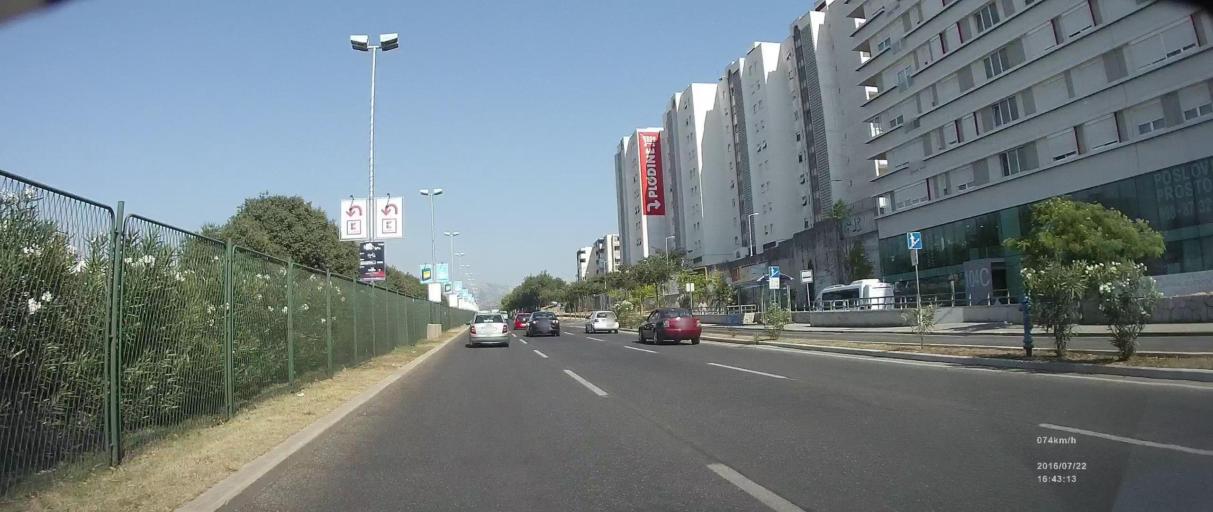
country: HR
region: Splitsko-Dalmatinska
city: Vranjic
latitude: 43.5197
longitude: 16.4663
